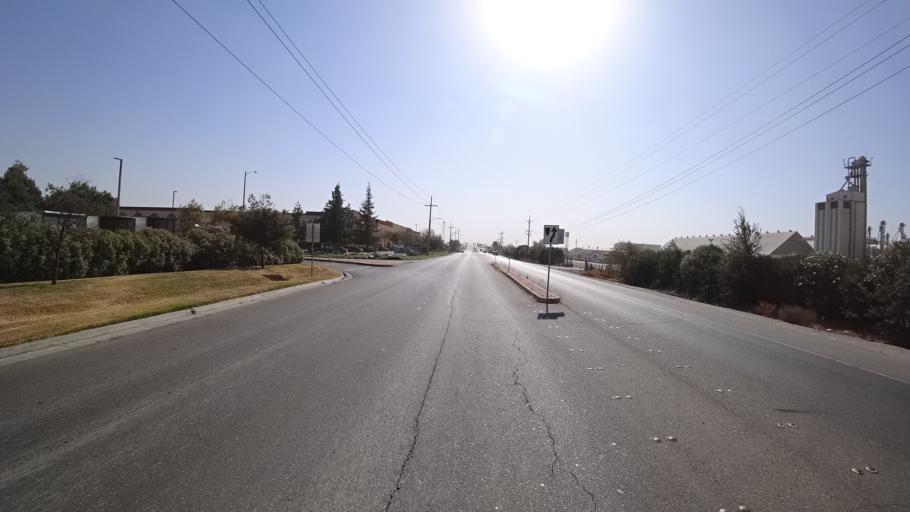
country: US
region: California
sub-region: Yolo County
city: Woodland
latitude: 38.6801
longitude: -121.7285
